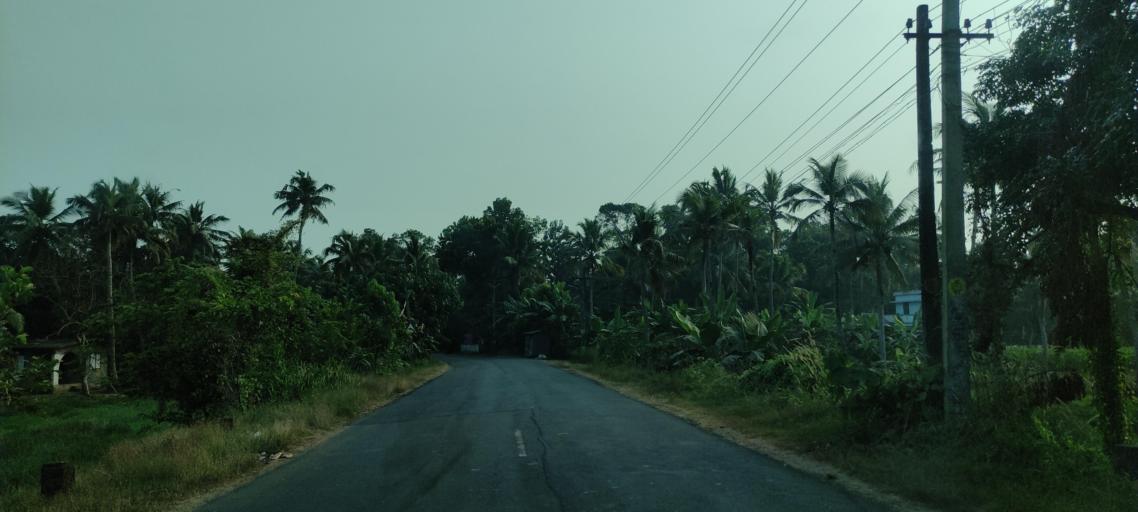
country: IN
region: Kerala
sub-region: Kottayam
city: Vaikam
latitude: 9.6901
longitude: 76.4636
